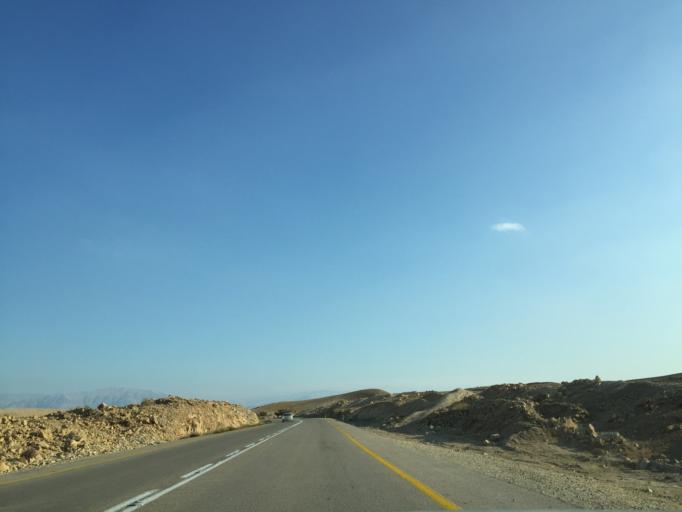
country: IL
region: Southern District
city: `En Boqeq
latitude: 31.1642
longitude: 35.3220
